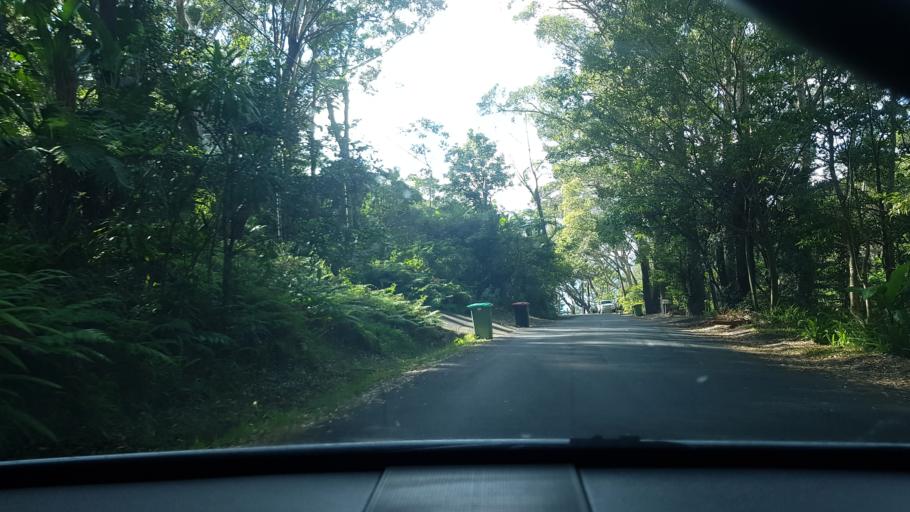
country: AU
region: New South Wales
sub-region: Gosford Shire
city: Macmasters Beach
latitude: -33.4990
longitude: 151.4210
